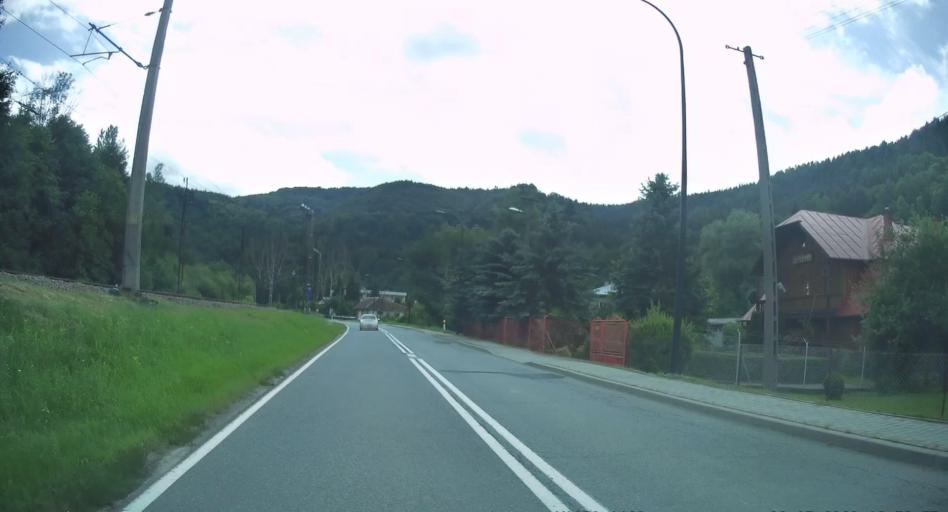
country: PL
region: Lesser Poland Voivodeship
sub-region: Powiat nowosadecki
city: Piwniczna-Zdroj
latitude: 49.3653
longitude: 20.7829
